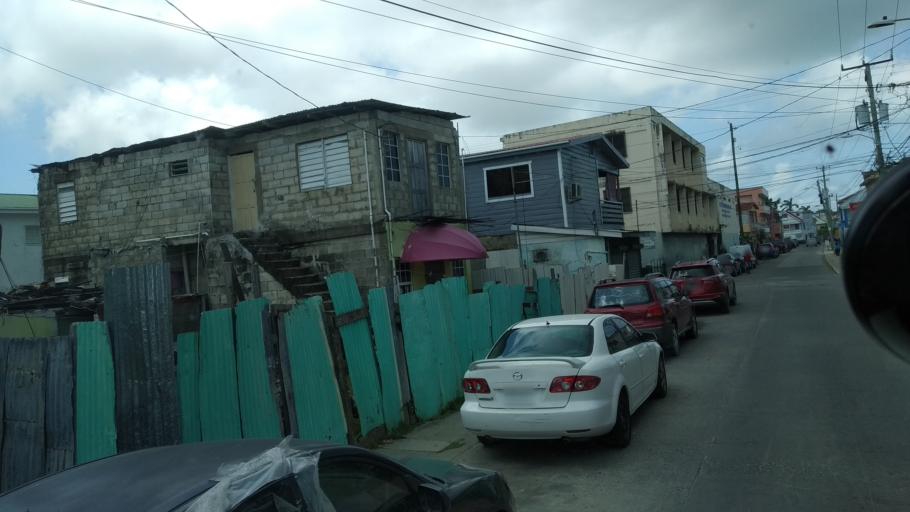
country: BZ
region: Belize
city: Belize City
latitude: 17.4985
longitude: -88.1873
